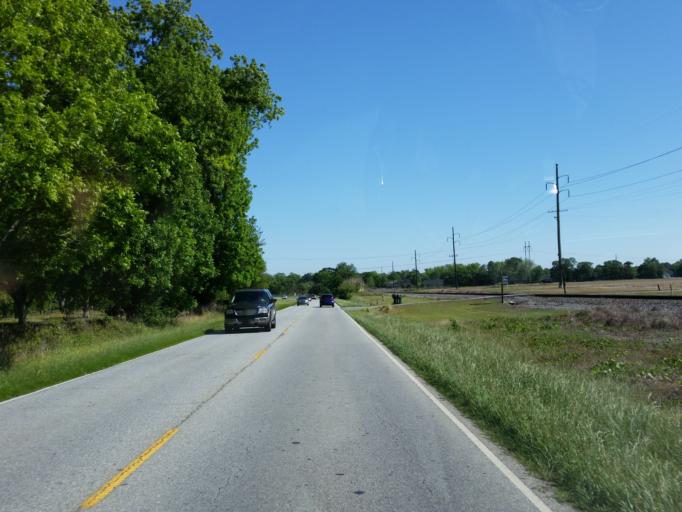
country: US
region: Georgia
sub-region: Lowndes County
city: Remerton
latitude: 30.9132
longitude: -83.3463
